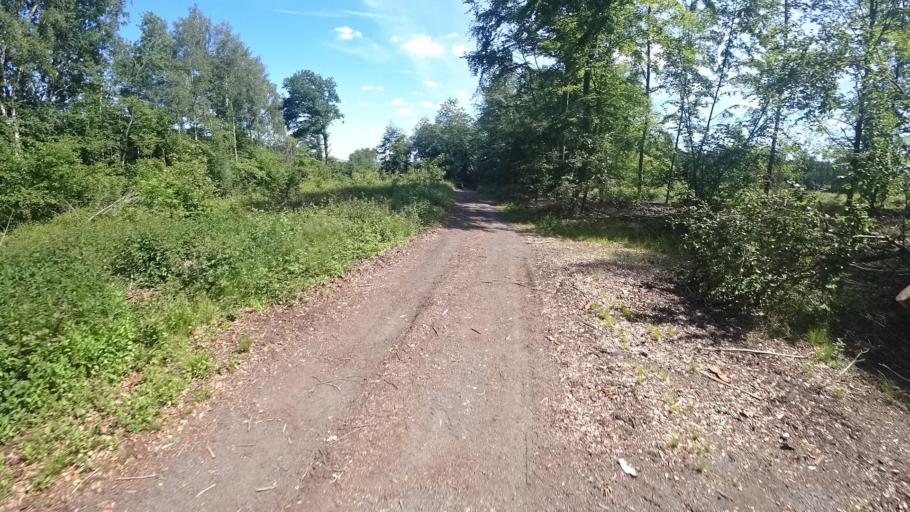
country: DE
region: Rheinland-Pfalz
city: Sorth
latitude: 50.6941
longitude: 7.6759
